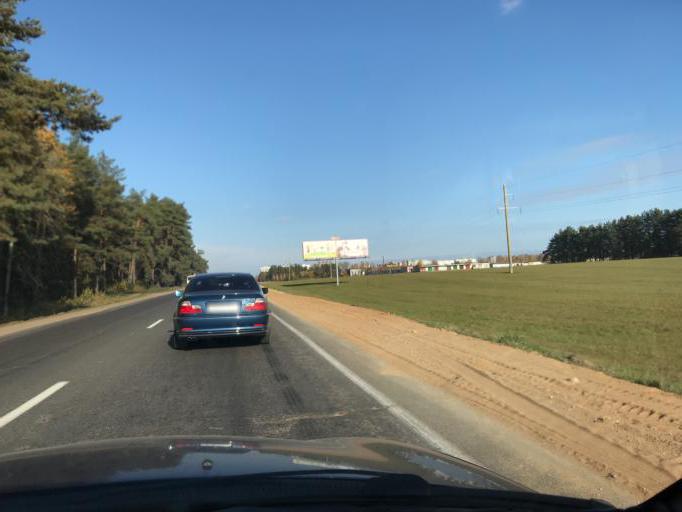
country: BY
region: Grodnenskaya
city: Lida
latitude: 53.8819
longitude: 25.2560
